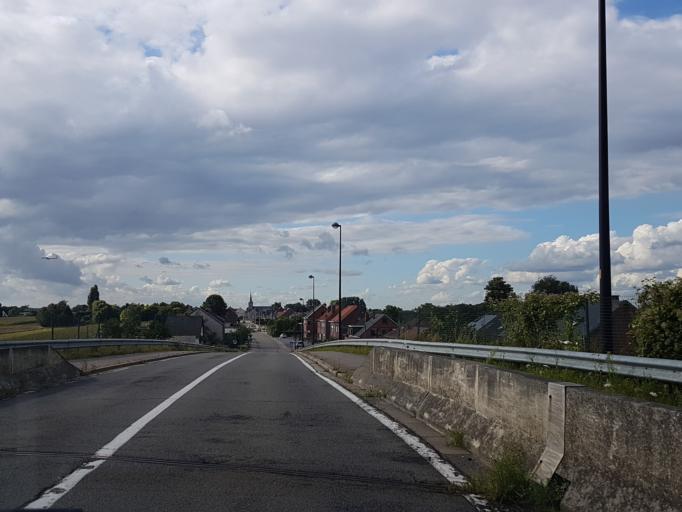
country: BE
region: Flanders
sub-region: Provincie Vlaams-Brabant
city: Kortenberg
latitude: 50.8949
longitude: 4.5666
